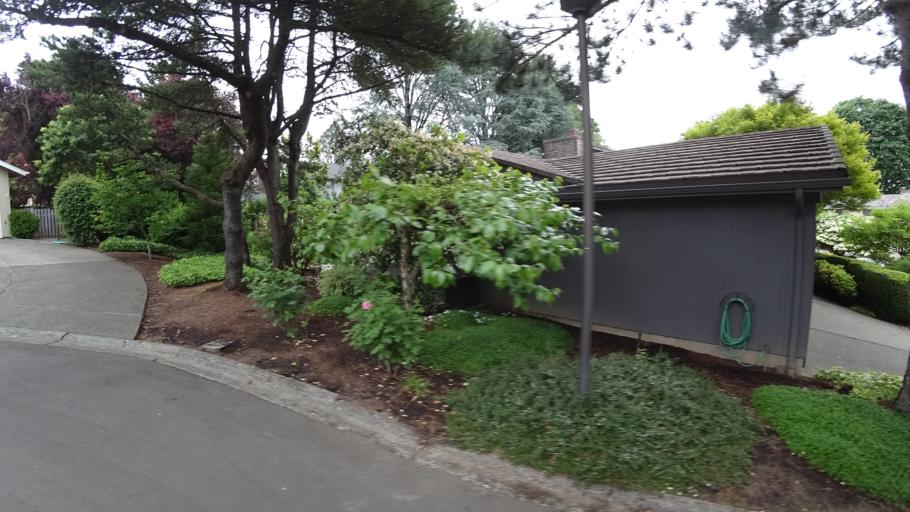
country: US
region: Oregon
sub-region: Clackamas County
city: Lake Oswego
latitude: 45.4298
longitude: -122.7093
